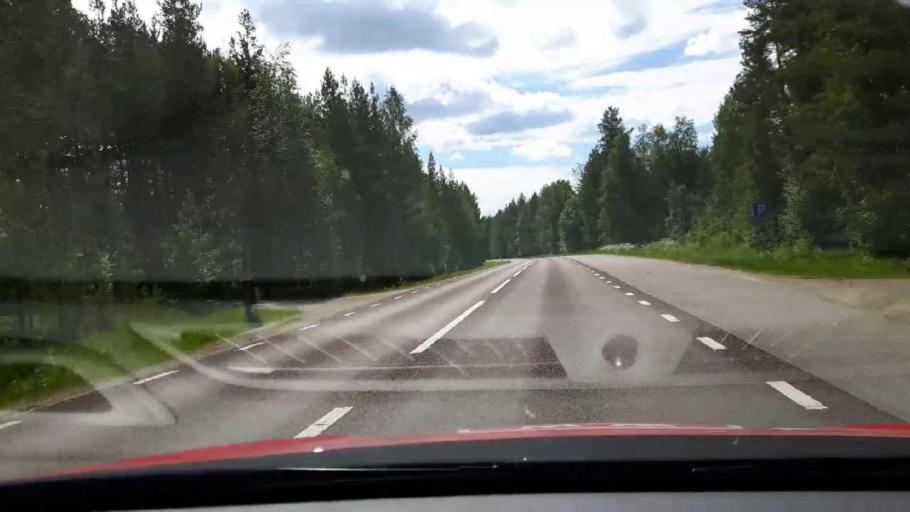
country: SE
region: Jaemtland
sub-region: Harjedalens Kommun
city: Sveg
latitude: 62.1522
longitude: 14.9534
